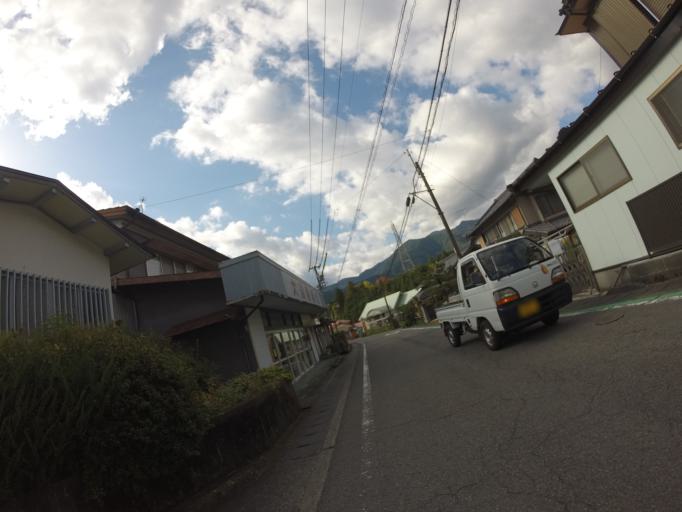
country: JP
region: Shizuoka
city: Kanaya
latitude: 35.0759
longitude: 138.1152
